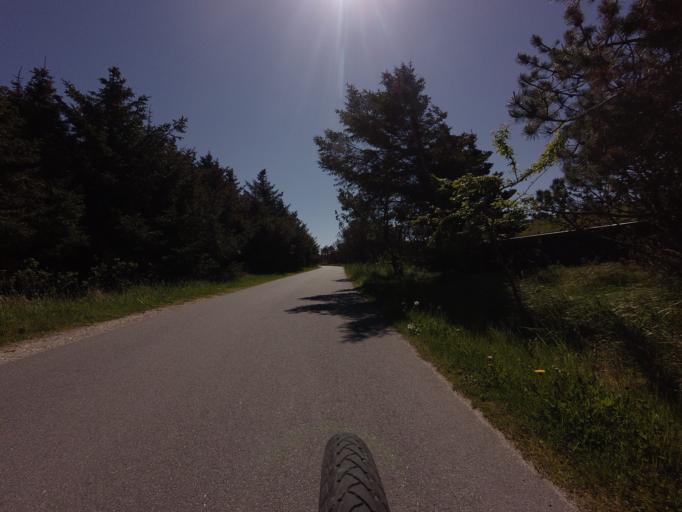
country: DK
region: North Denmark
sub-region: Jammerbugt Kommune
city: Pandrup
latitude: 57.2307
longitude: 9.5599
